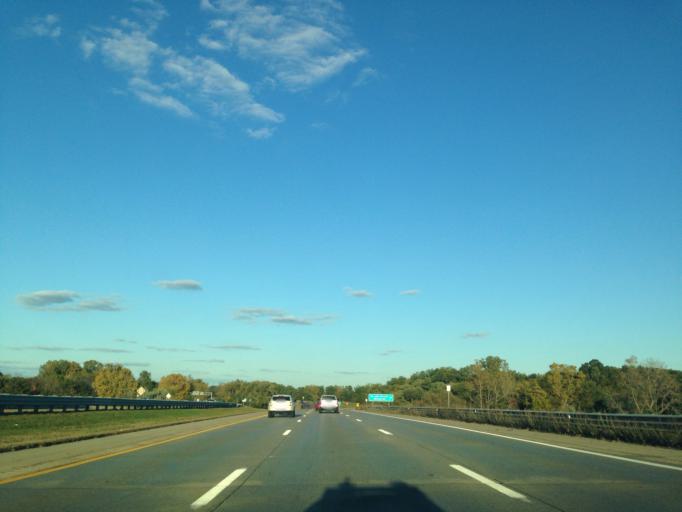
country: US
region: Michigan
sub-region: Oakland County
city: Bloomfield Hills
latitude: 42.6045
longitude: -83.2478
